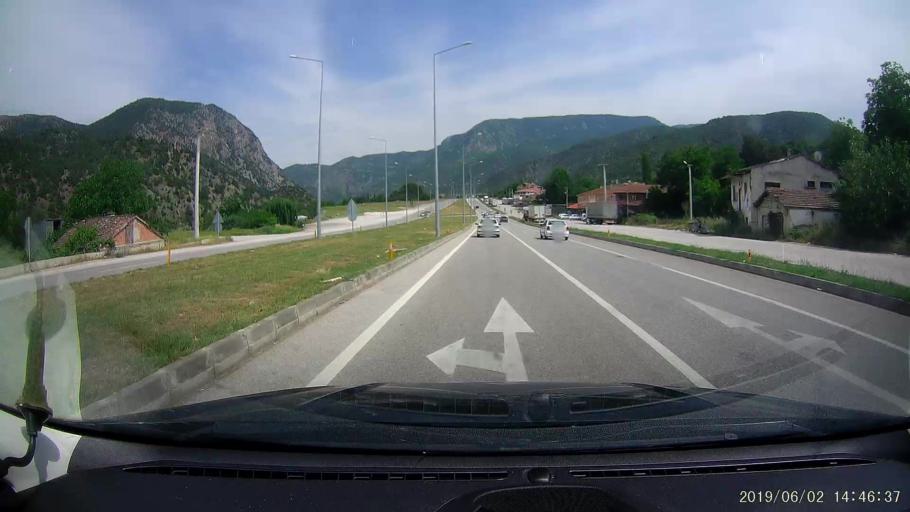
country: TR
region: Corum
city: Hacihamza
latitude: 41.0757
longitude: 34.4514
